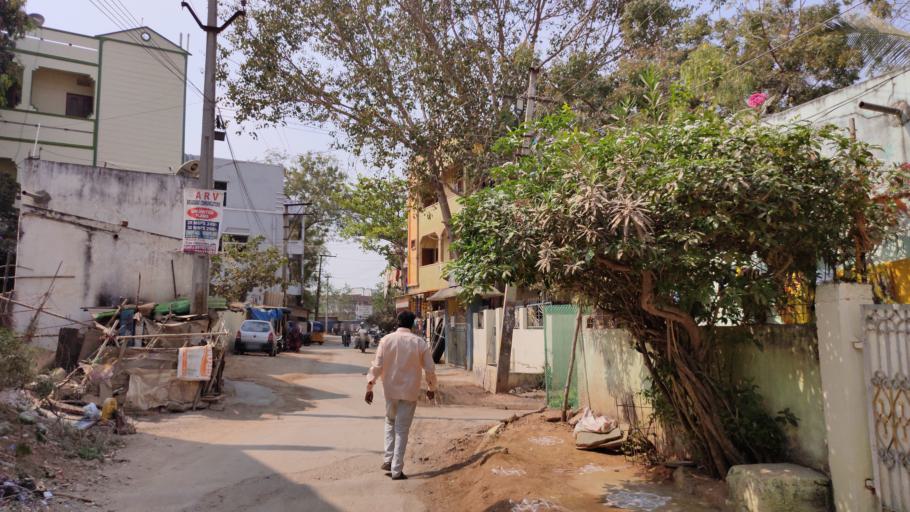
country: IN
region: Telangana
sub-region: Rangareddi
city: Quthbullapur
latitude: 17.4922
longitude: 78.4629
